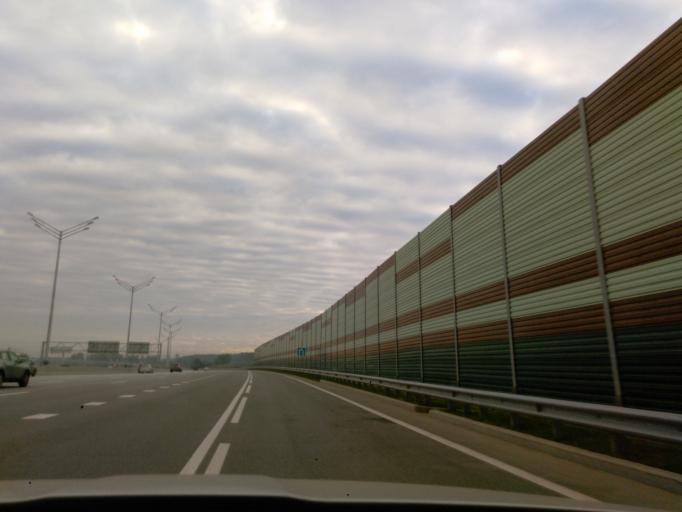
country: RU
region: Moskovskaya
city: Novopodrezkovo
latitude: 55.9561
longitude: 37.3687
